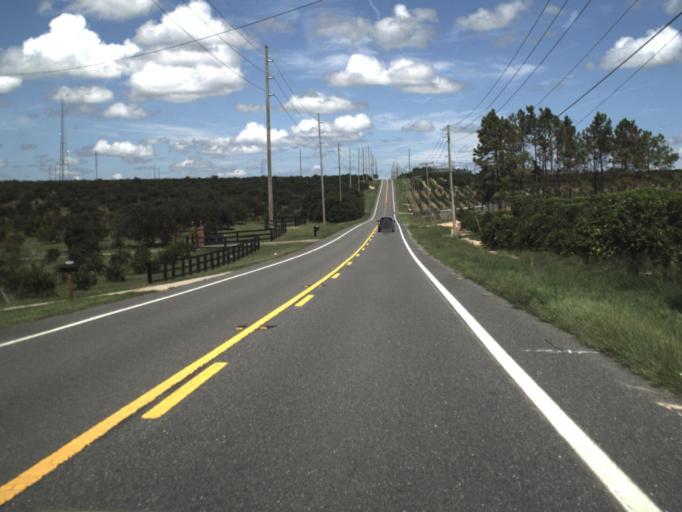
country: US
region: Florida
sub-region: Polk County
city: Dundee
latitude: 27.9977
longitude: -81.5950
